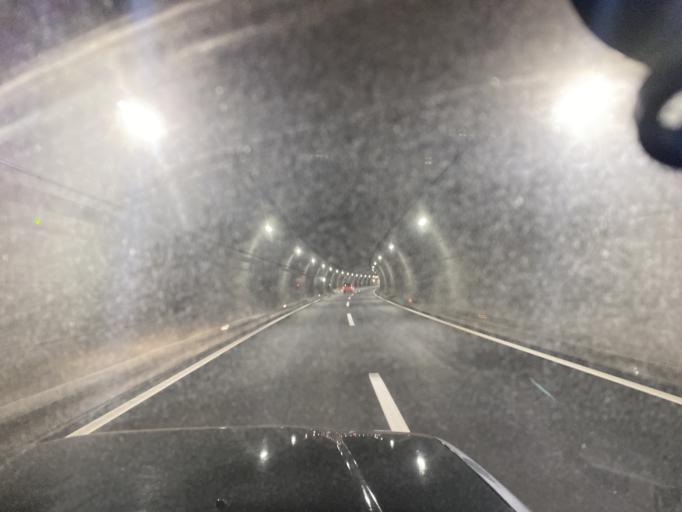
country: JP
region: Gifu
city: Gujo
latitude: 36.0187
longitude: 136.9786
